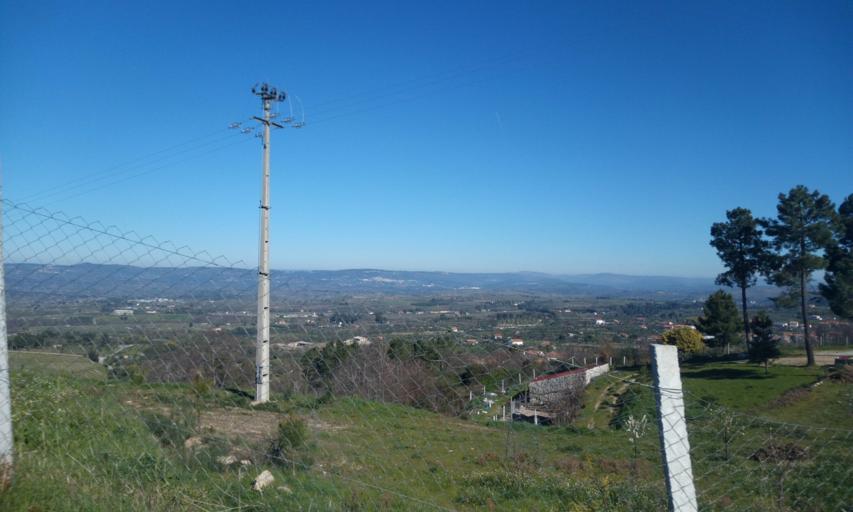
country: PT
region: Guarda
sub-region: Fornos de Algodres
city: Fornos de Algodres
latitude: 40.5154
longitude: -7.5617
